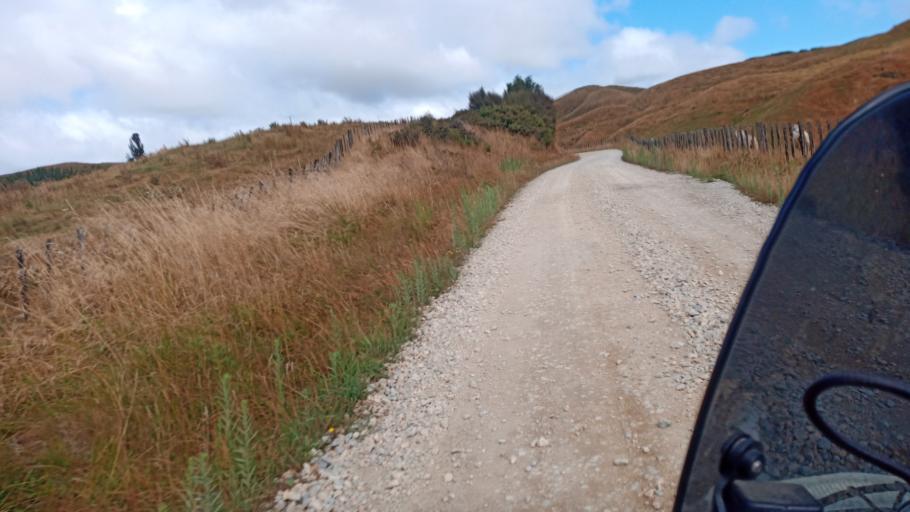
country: NZ
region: Hawke's Bay
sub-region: Wairoa District
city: Wairoa
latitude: -38.6036
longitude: 177.4702
